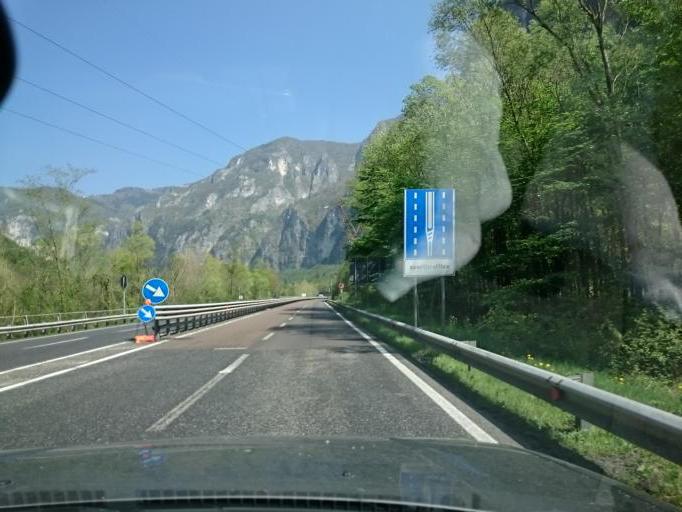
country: IT
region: Veneto
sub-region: Provincia di Vicenza
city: Cismon del Grappa
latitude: 45.9019
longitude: 11.7067
